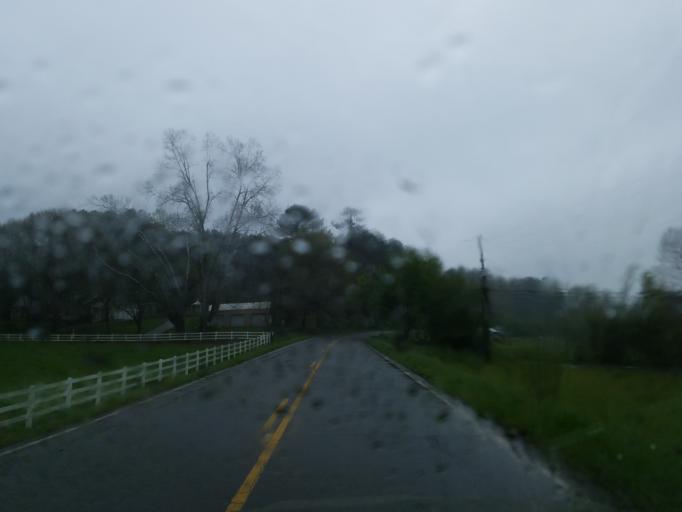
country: US
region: Georgia
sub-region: Gilmer County
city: Ellijay
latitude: 34.5901
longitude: -84.5328
